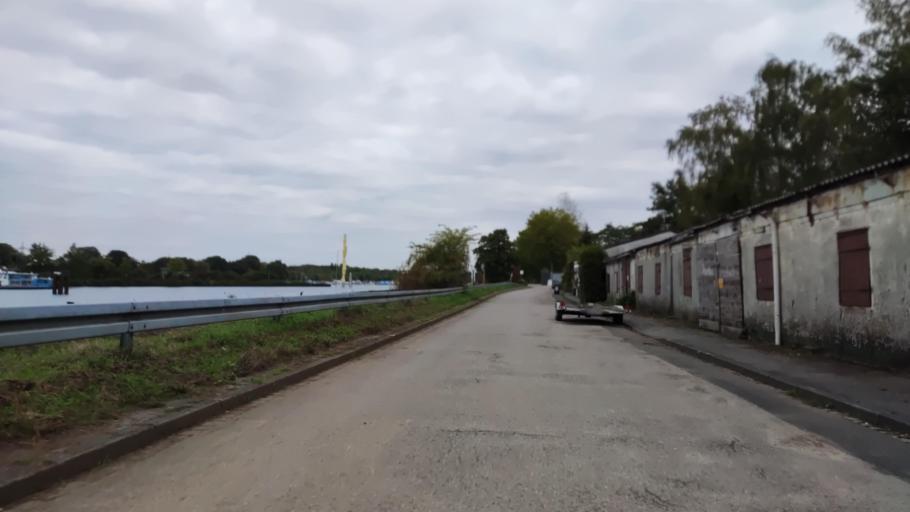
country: DE
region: North Rhine-Westphalia
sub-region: Regierungsbezirk Arnsberg
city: Herne
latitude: 51.5624
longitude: 7.2486
